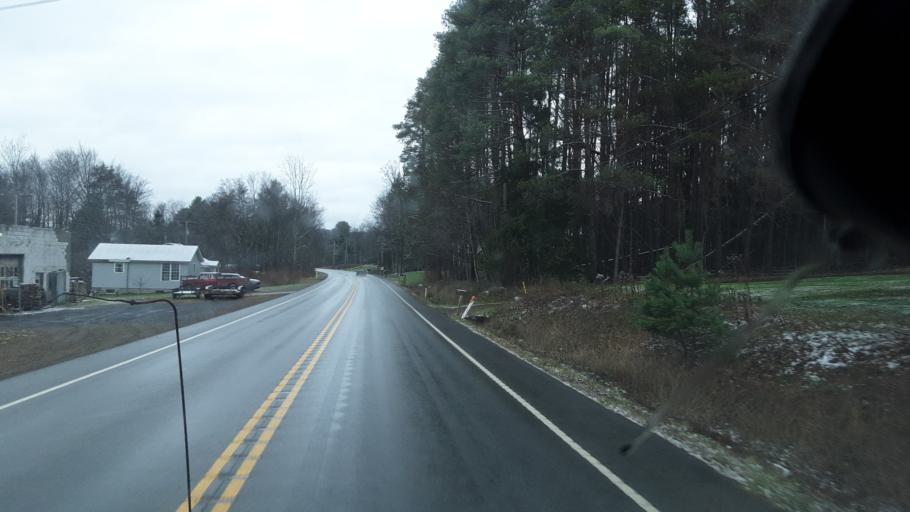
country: US
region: Pennsylvania
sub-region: Potter County
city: Shinglehouse
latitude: 41.9342
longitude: -78.1278
